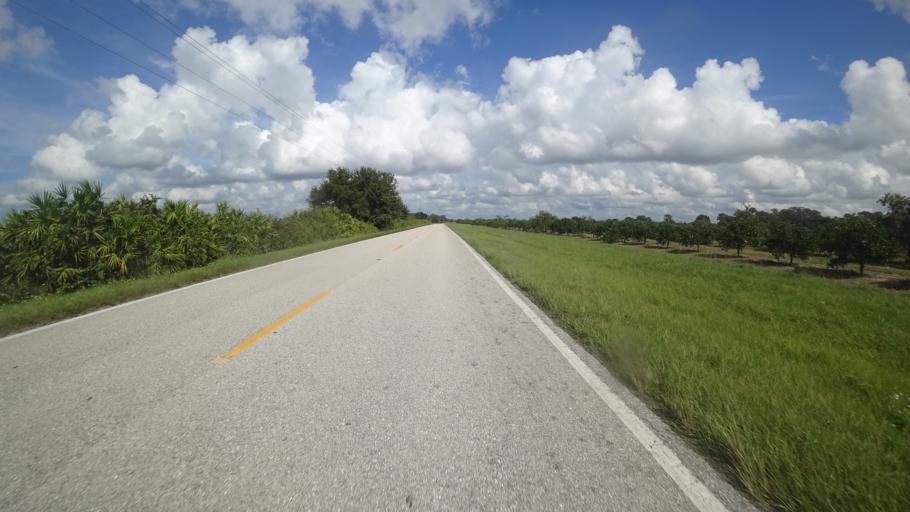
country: US
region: Florida
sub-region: Hillsborough County
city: Wimauma
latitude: 27.5714
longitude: -82.1046
